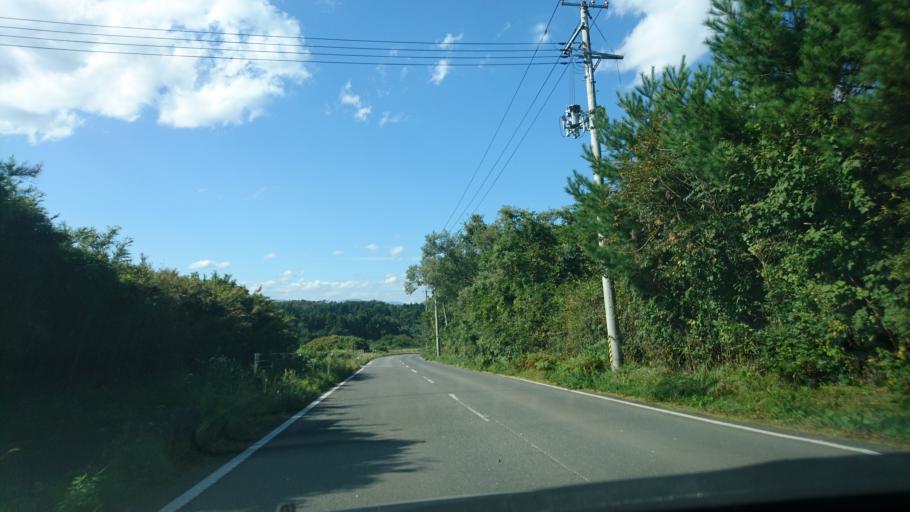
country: JP
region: Iwate
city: Ichinoseki
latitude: 38.8563
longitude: 141.0526
